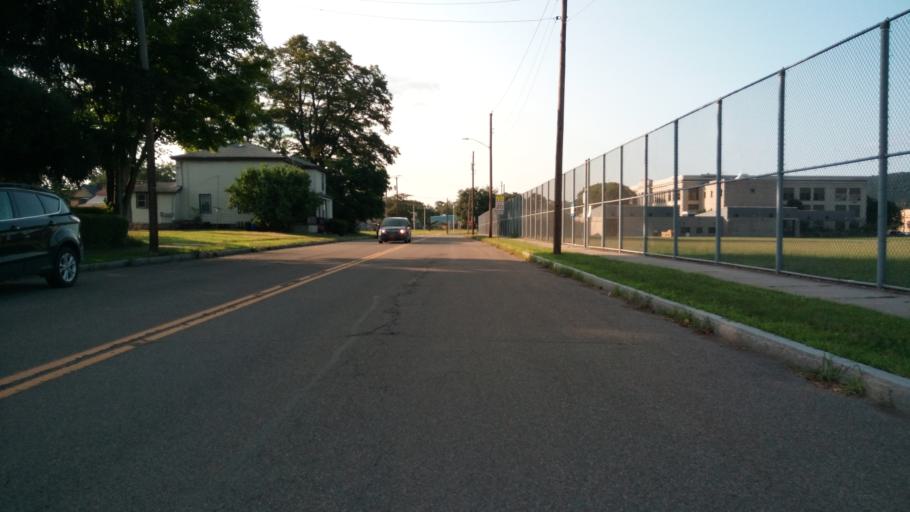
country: US
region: New York
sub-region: Chemung County
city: Elmira
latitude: 42.0941
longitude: -76.8039
